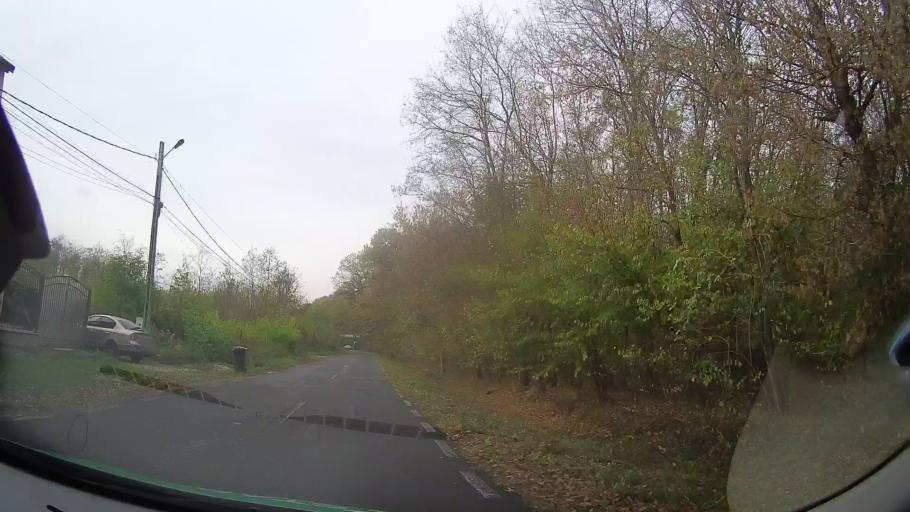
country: RO
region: Ilfov
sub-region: Comuna Snagov
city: Snagov
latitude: 44.7167
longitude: 26.1903
